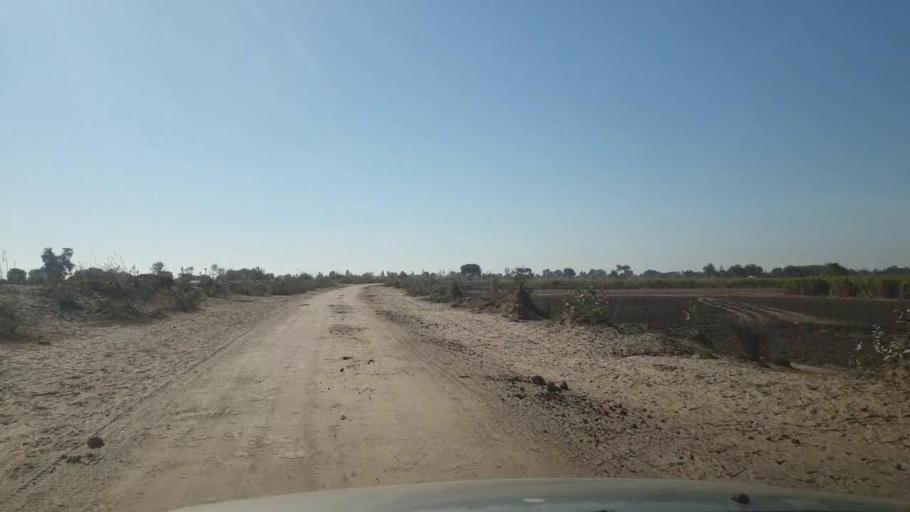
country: PK
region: Sindh
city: Ghotki
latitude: 28.0208
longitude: 69.2681
